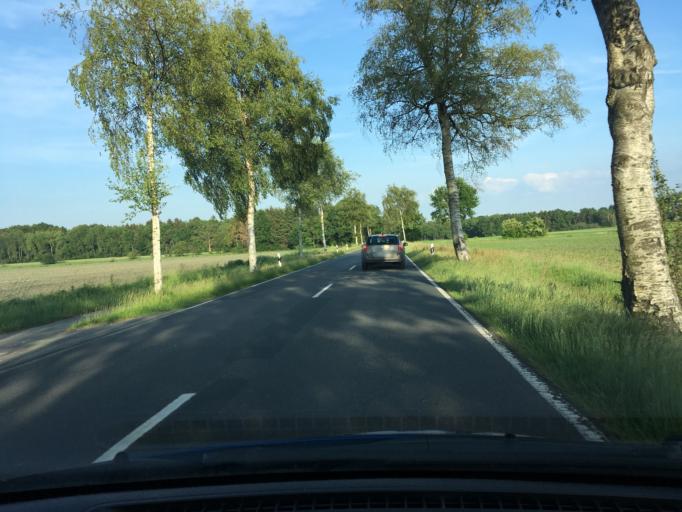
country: DE
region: Lower Saxony
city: Otter
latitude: 53.2537
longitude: 9.7587
